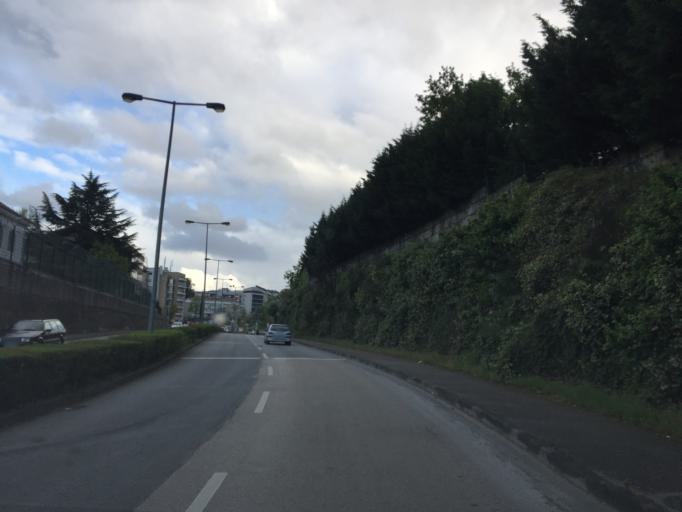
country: PT
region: Viseu
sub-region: Viseu
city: Viseu
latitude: 40.6613
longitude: -7.9241
